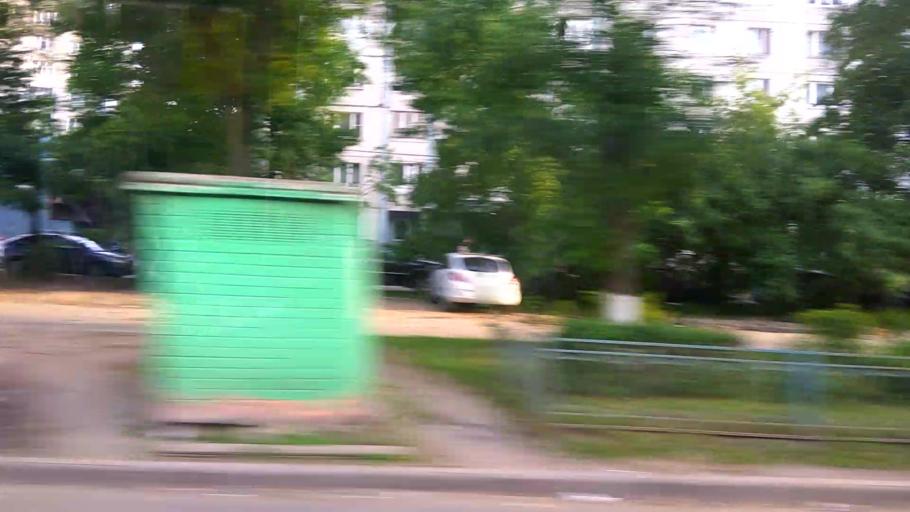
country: RU
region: Moskovskaya
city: Yubileyny
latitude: 55.9236
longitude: 37.8615
